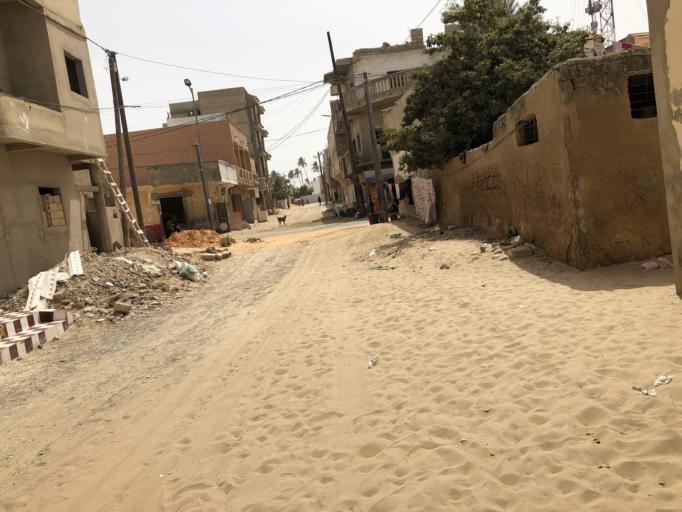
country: SN
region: Saint-Louis
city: Saint-Louis
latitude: 16.0179
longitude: -16.4856
